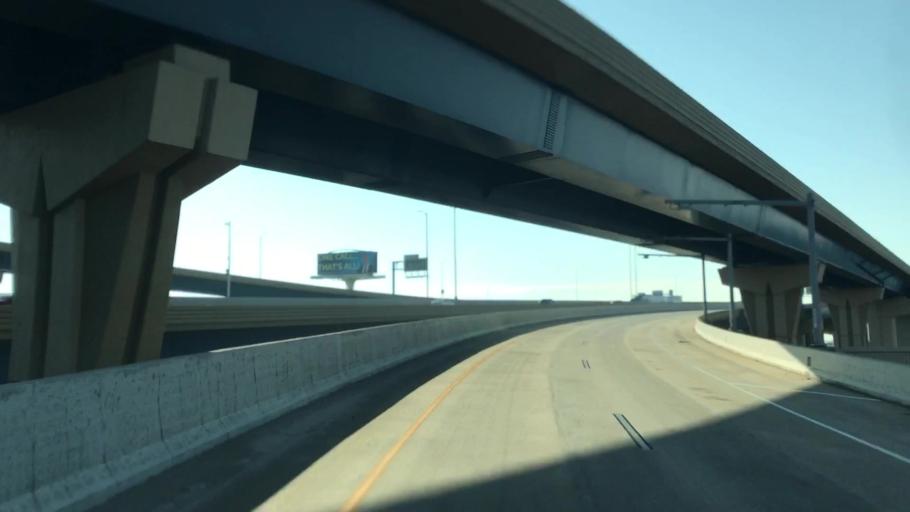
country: US
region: Wisconsin
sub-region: Milwaukee County
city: Milwaukee
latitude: 43.0342
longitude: -87.9238
